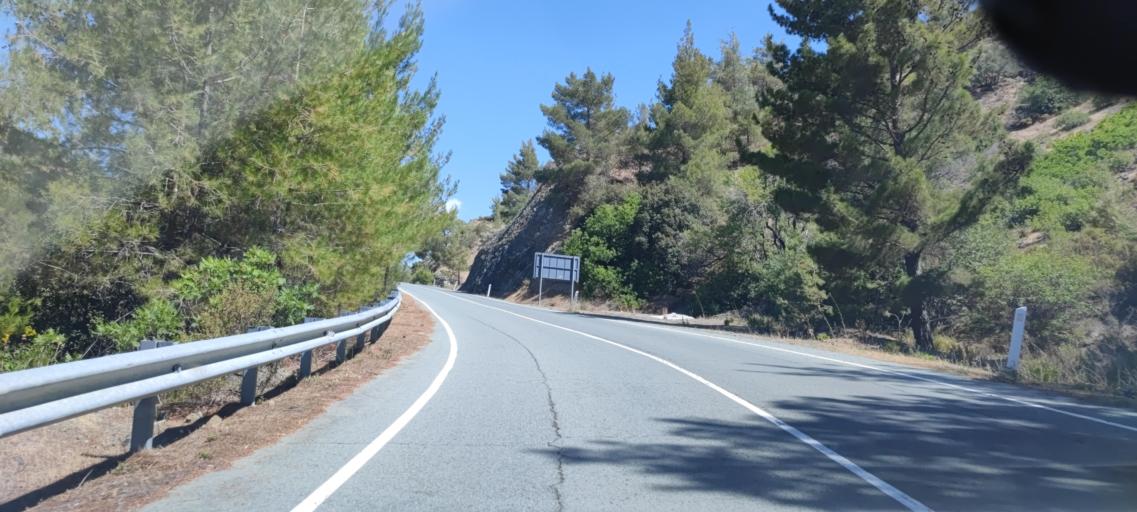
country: CY
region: Lefkosia
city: Kakopetria
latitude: 34.9144
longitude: 32.8152
